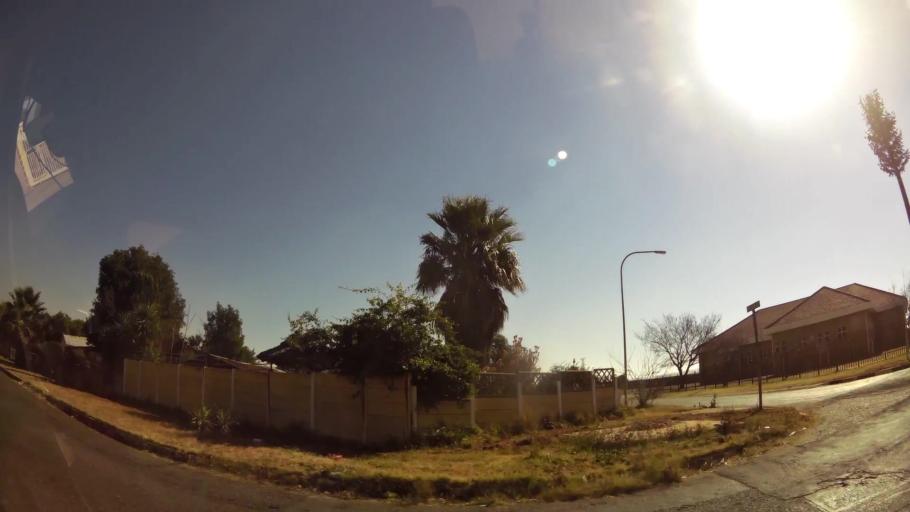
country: ZA
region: Gauteng
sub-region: City of Johannesburg Metropolitan Municipality
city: Roodepoort
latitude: -26.1804
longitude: 27.9537
